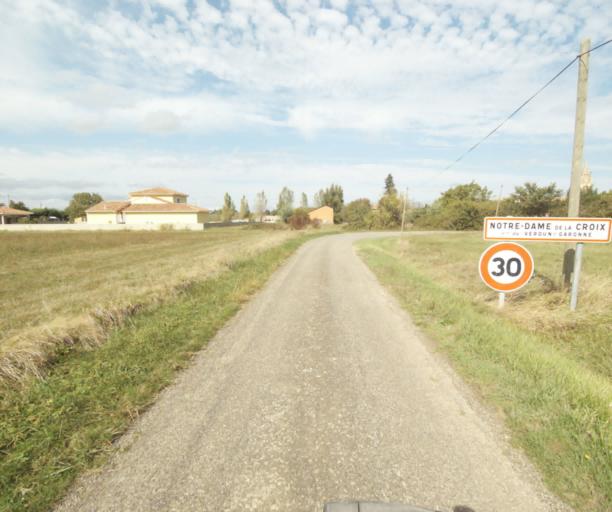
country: FR
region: Midi-Pyrenees
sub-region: Departement du Tarn-et-Garonne
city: Verdun-sur-Garonne
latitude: 43.8609
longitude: 1.1765
